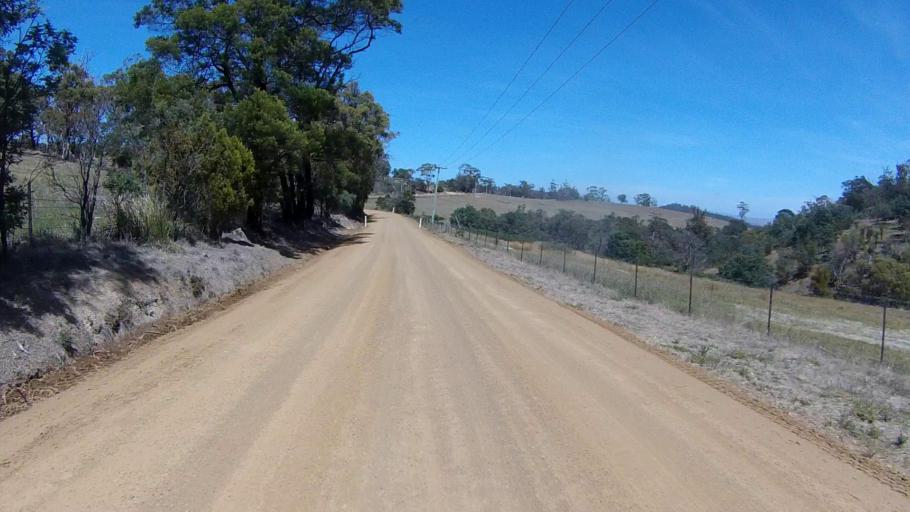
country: AU
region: Tasmania
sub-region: Sorell
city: Sorell
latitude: -42.7797
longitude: 147.6496
